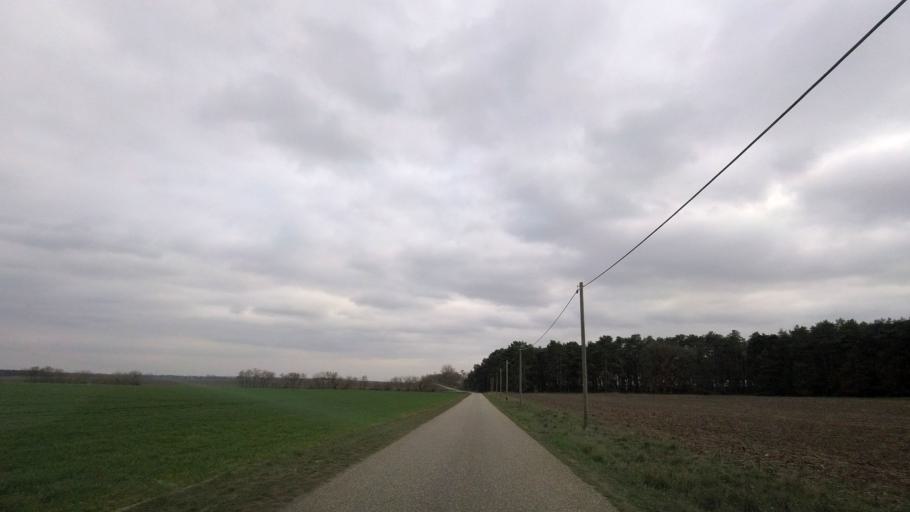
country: DE
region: Saxony-Anhalt
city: Seyda
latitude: 51.9079
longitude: 12.8877
